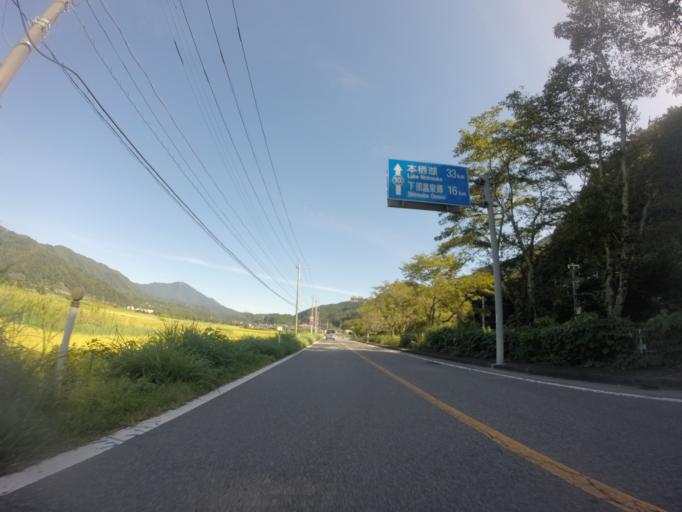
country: JP
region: Shizuoka
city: Fujinomiya
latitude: 35.3251
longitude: 138.4514
